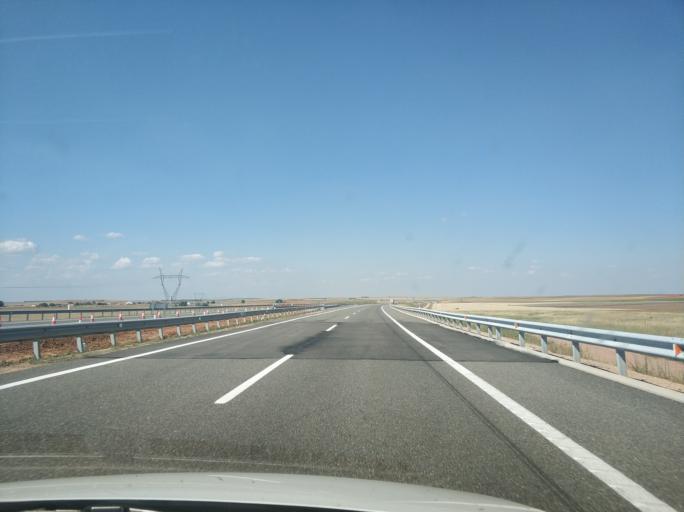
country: ES
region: Castille and Leon
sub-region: Provincia de Zamora
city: San Cebrian de Castro
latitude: 41.7405
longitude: -5.7671
